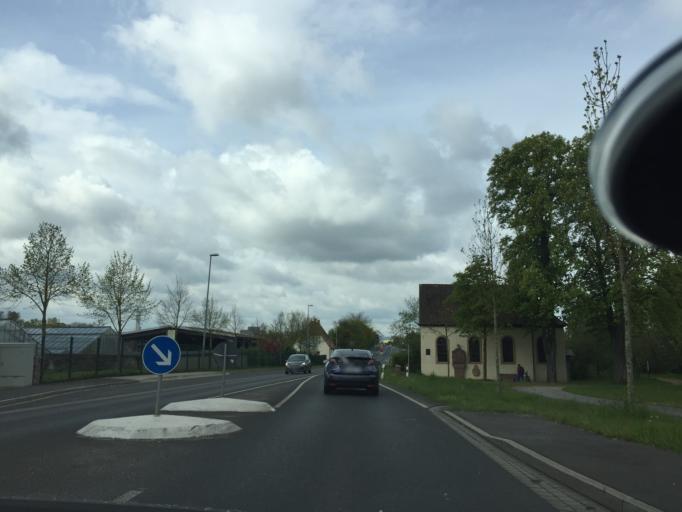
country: DE
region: Bavaria
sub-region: Regierungsbezirk Unterfranken
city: Mainaschaff
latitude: 49.9510
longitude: 9.1102
